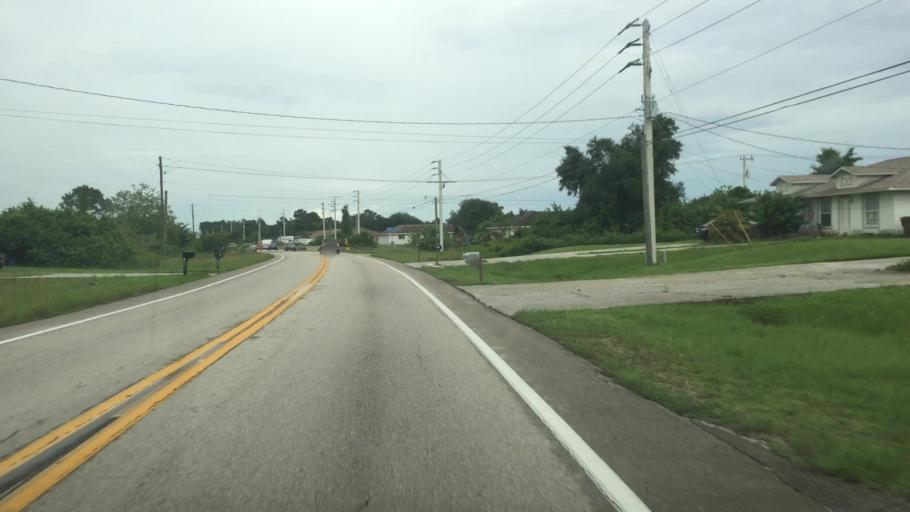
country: US
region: Florida
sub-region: Lee County
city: Gateway
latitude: 26.5987
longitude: -81.7326
